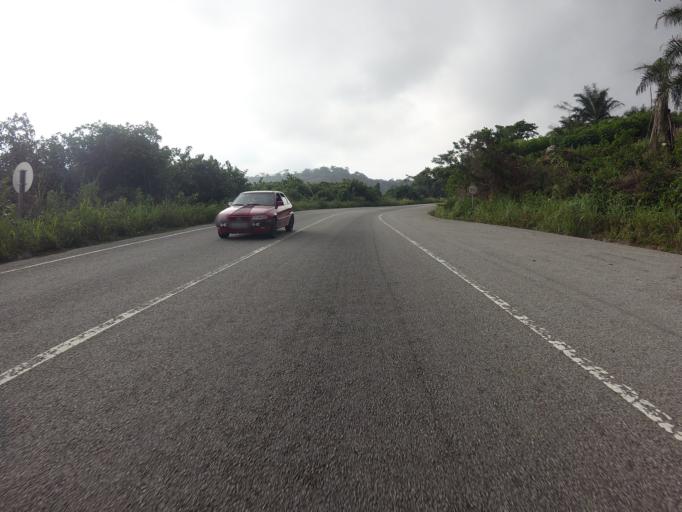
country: GH
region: Volta
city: Ho
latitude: 6.8143
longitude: 0.4205
